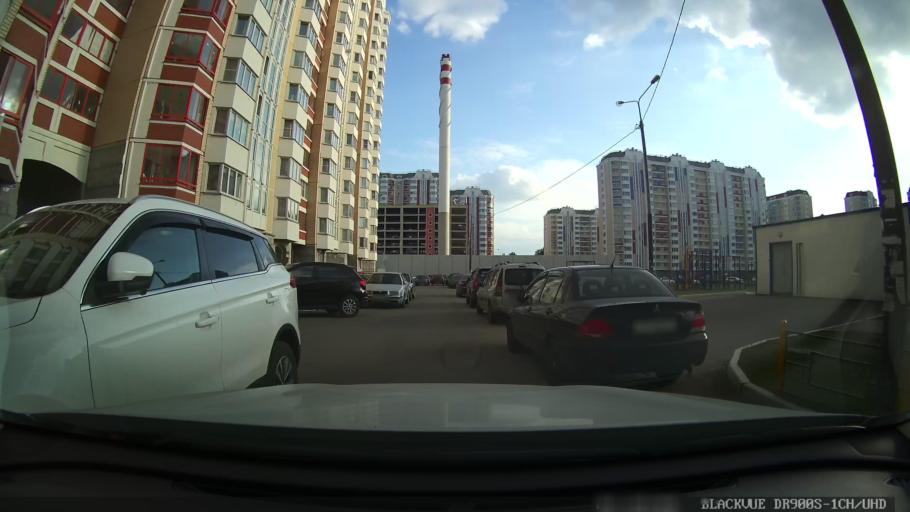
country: RU
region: Moskovskaya
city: Nemchinovka
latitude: 55.7268
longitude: 37.3568
